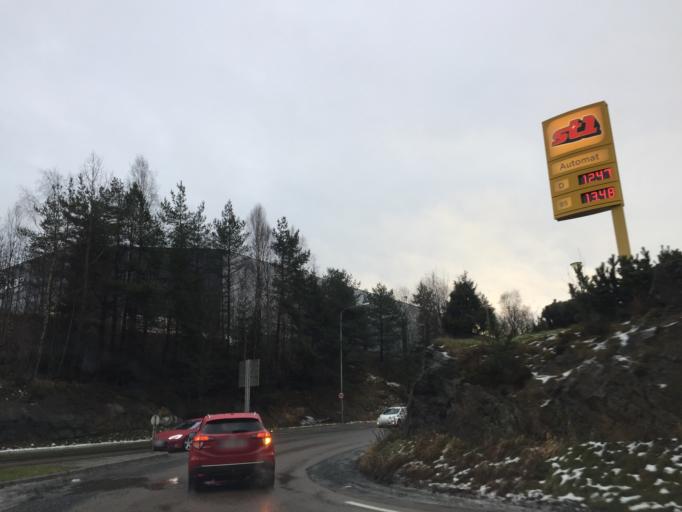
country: NO
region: Ostfold
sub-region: Moss
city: Moss
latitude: 59.4455
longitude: 10.6997
